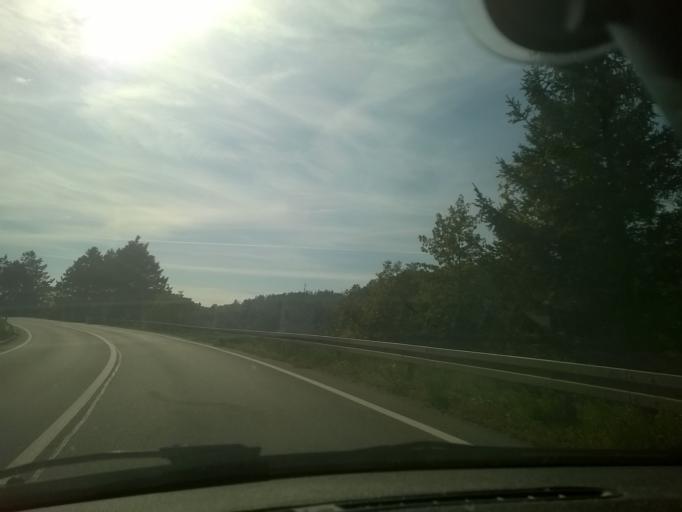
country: HR
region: Krapinsko-Zagorska
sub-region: Grad Krapina
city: Krapina
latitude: 46.1694
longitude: 15.8651
